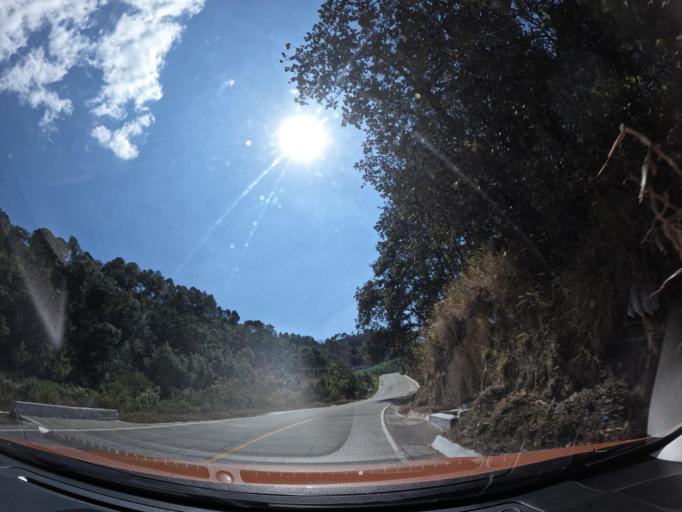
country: GT
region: Solola
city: San Antonio Palopo
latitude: 14.6947
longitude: -91.0713
